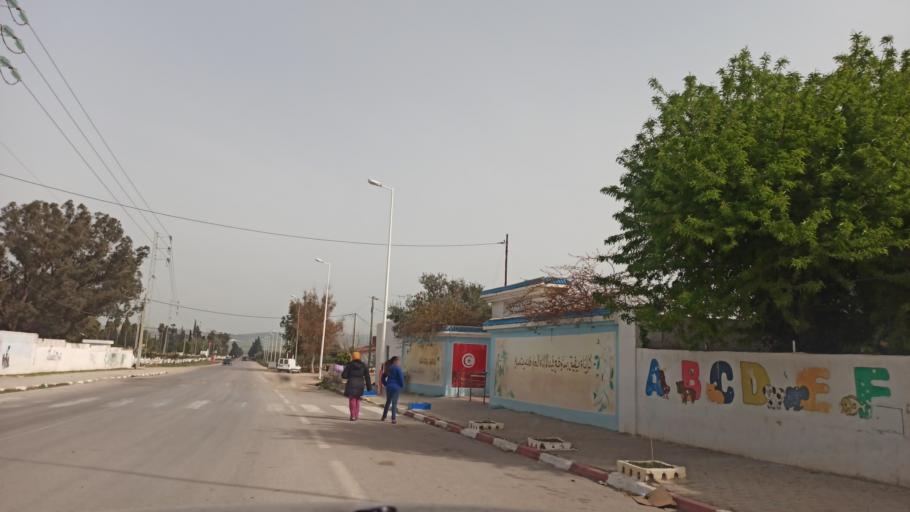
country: TN
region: Zaghwan
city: Zaghouan
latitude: 36.4238
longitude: 10.0936
